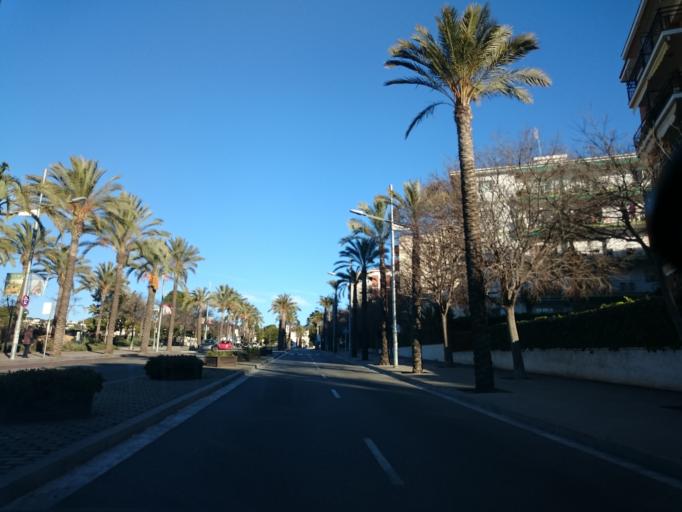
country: ES
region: Catalonia
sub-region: Provincia de Barcelona
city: Sitges
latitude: 41.2399
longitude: 1.8065
